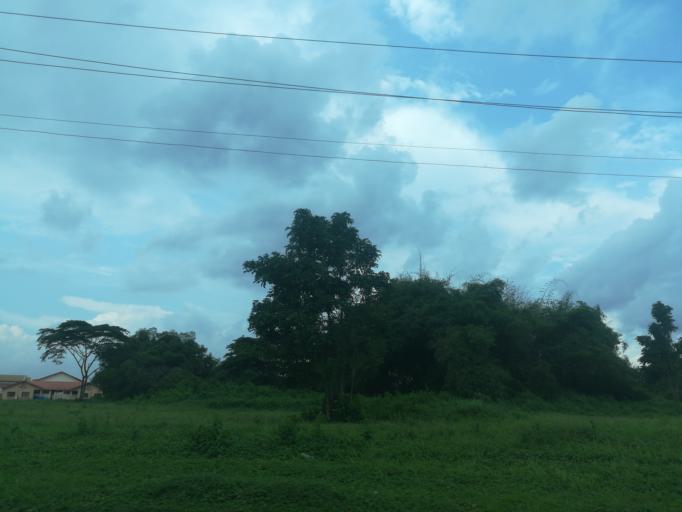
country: NG
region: Lagos
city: Ikorodu
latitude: 6.6360
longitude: 3.5221
